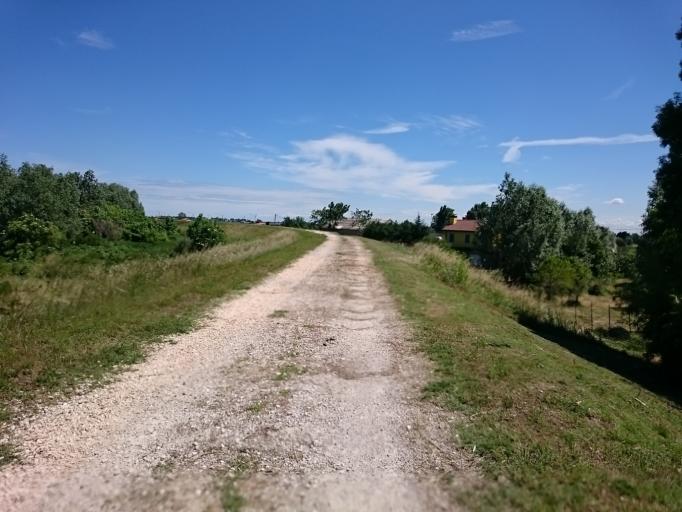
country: IT
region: Veneto
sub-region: Provincia di Padova
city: Correzzola
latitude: 45.2365
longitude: 12.0712
